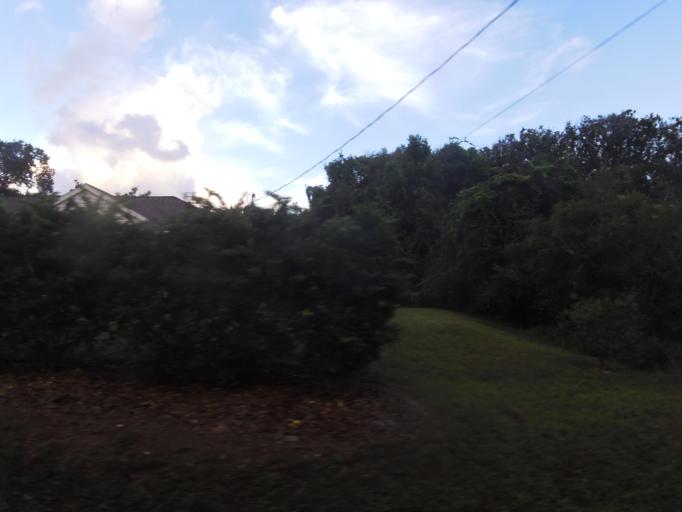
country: US
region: Florida
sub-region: Saint Johns County
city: Villano Beach
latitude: 29.9551
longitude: -81.3098
